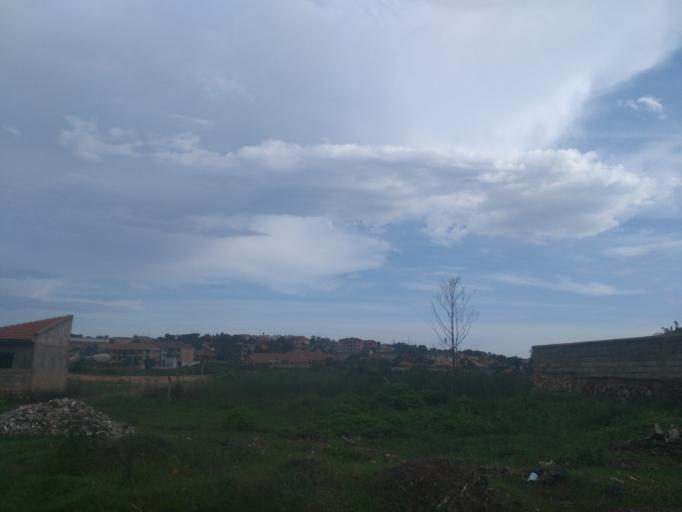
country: UG
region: Central Region
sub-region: Wakiso District
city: Kireka
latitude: 0.3787
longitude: 32.6185
